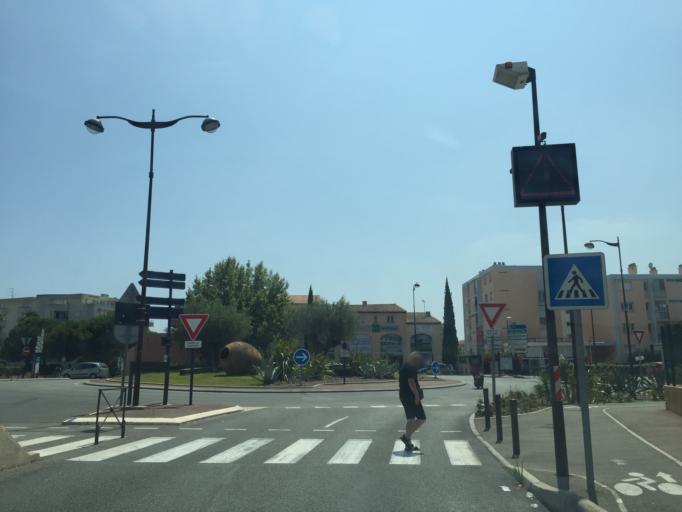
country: FR
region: Provence-Alpes-Cote d'Azur
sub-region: Departement du Var
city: Frejus
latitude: 43.4278
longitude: 6.7490
